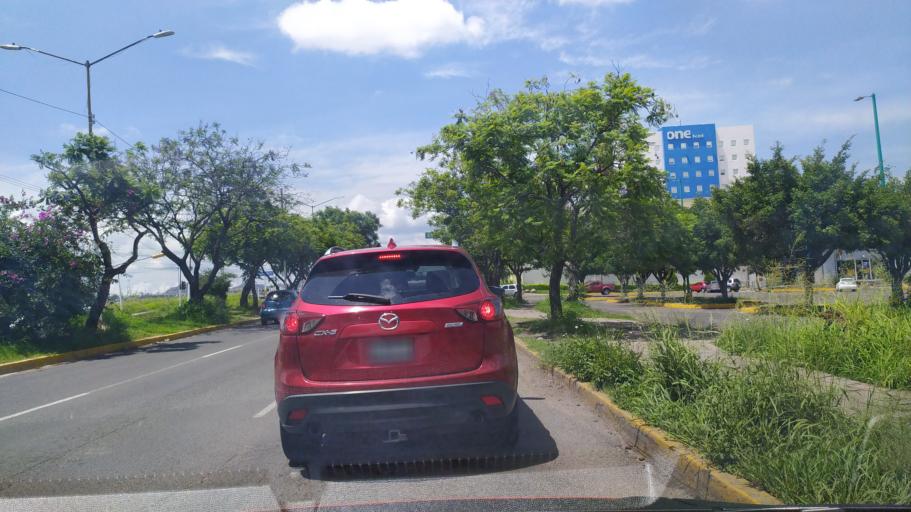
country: MX
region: Jalisco
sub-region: Zapopan
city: Zapopan
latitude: 20.7426
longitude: -103.3867
